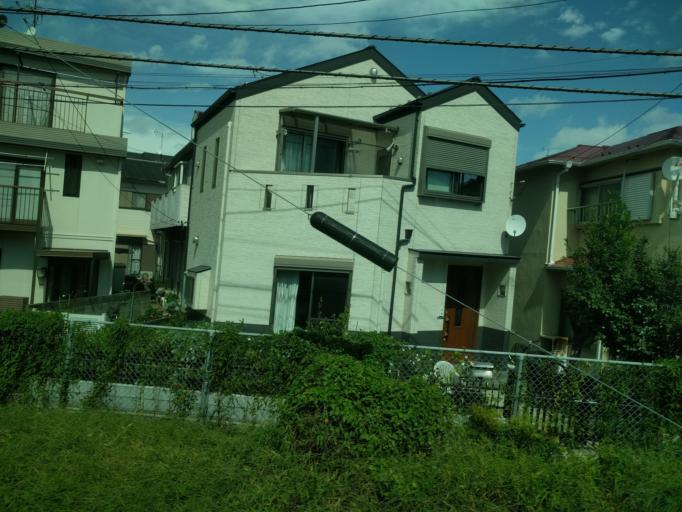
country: JP
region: Tokyo
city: Chofugaoka
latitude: 35.6153
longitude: 139.5800
